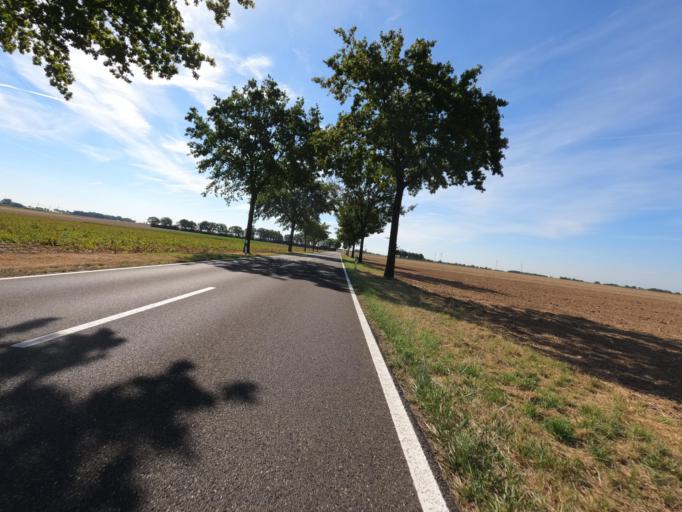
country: DE
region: North Rhine-Westphalia
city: Erkelenz
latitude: 51.0508
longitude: 6.3488
